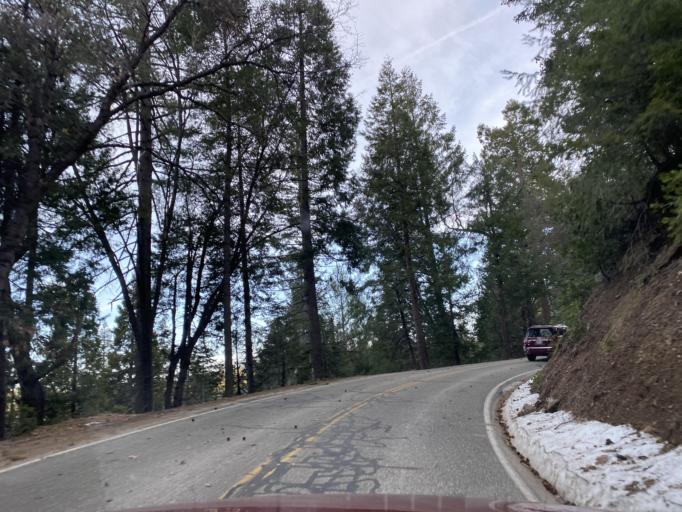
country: US
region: California
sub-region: Amador County
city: Pioneer
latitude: 38.5129
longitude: -120.4878
